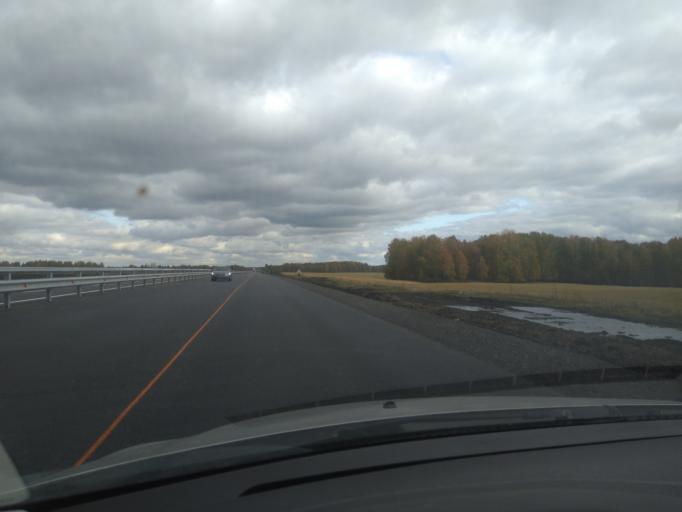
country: RU
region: Sverdlovsk
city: Pyshma
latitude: 56.8953
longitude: 63.0545
